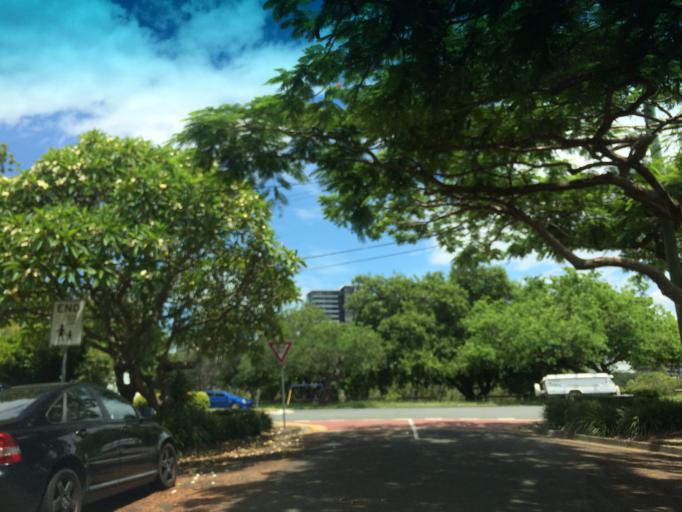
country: AU
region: Queensland
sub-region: Brisbane
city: Toowong
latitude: -27.4876
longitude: 152.9974
